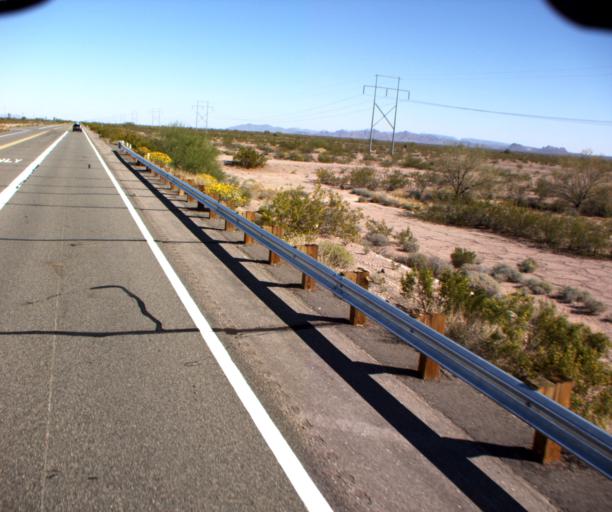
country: US
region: Arizona
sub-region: La Paz County
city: Quartzsite
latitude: 33.3386
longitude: -114.2170
